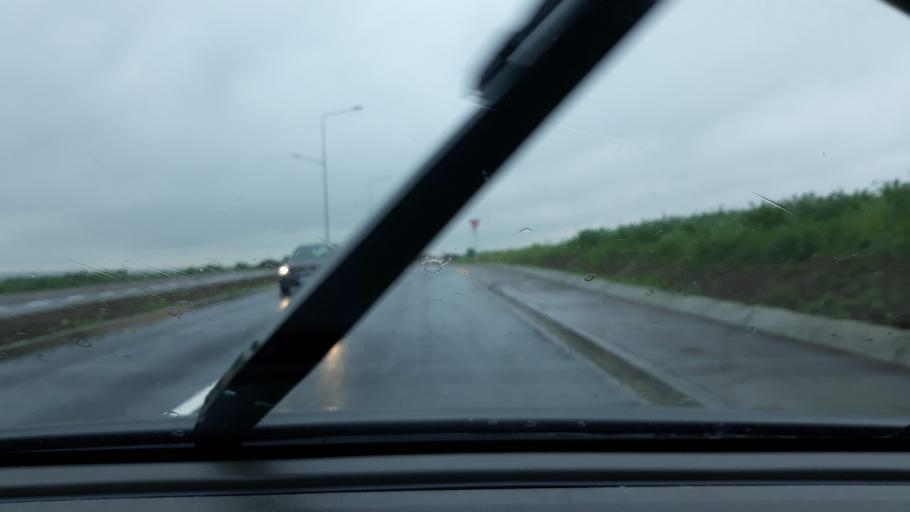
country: RO
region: Bihor
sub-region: Comuna Biharea
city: Biharea
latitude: 47.1070
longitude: 21.9068
